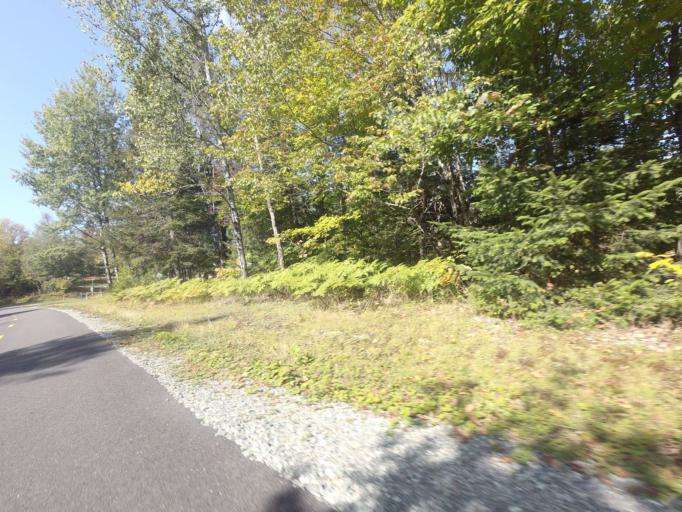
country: CA
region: Quebec
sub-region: Laurentides
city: Mont-Tremblant
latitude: 46.1339
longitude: -74.4878
